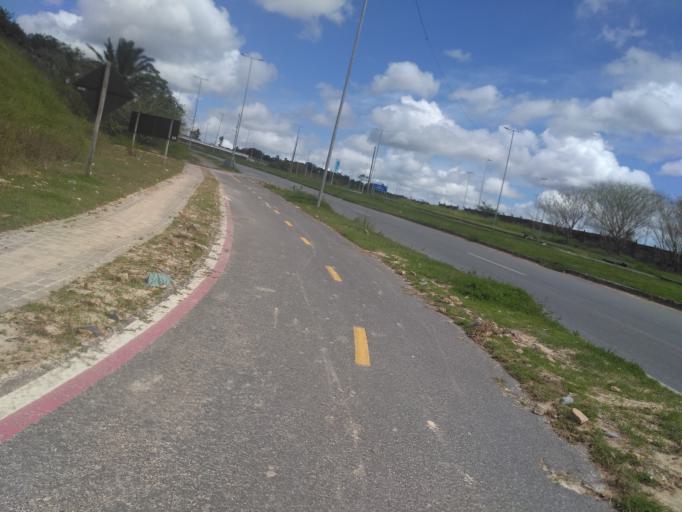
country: BR
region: Pernambuco
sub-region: Sao Lourenco Da Mata
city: Sao Lourenco da Mata
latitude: -8.0434
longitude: -35.0092
